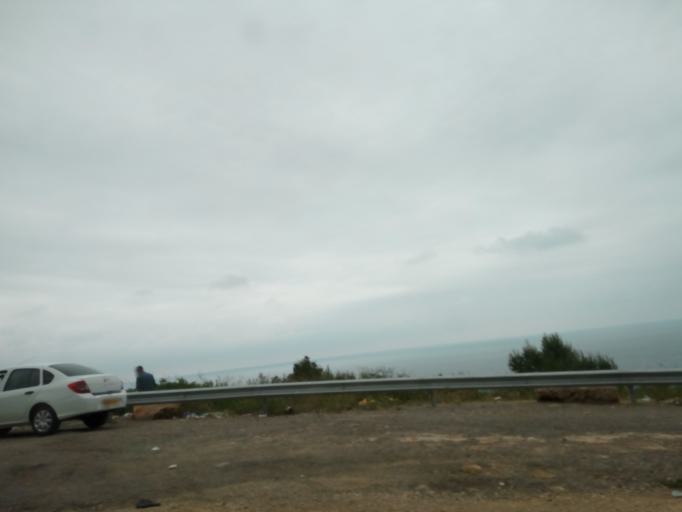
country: DZ
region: Tipaza
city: Tipasa
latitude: 36.5882
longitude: 2.5508
